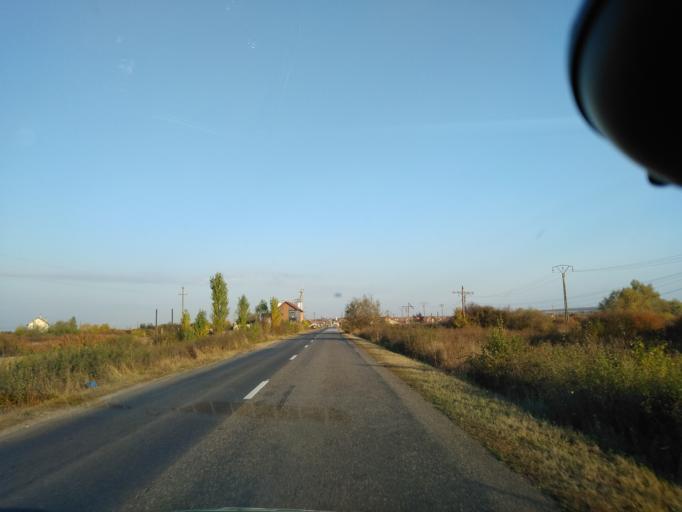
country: RO
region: Timis
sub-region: Comuna Pischia
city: Pischia
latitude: 45.8933
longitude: 21.3461
